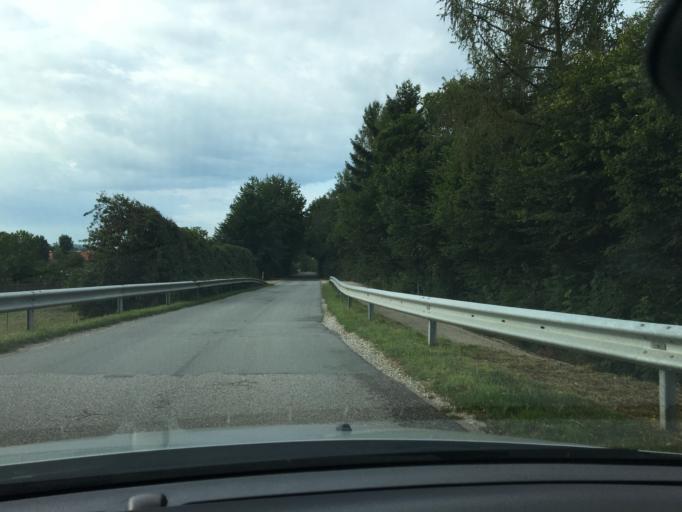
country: DE
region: Bavaria
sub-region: Upper Bavaria
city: Muehldorf
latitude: 48.2504
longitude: 12.5493
